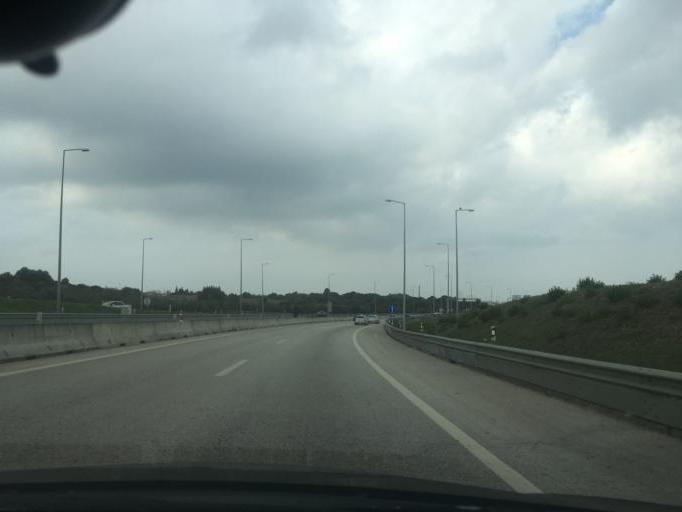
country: PT
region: Lisbon
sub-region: Sintra
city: Sintra
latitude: 38.8122
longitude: -9.3571
